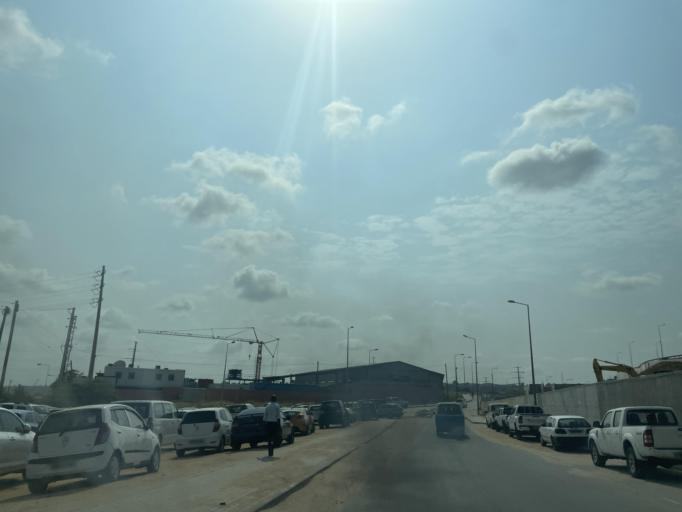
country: AO
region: Luanda
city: Luanda
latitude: -8.8036
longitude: 13.2497
